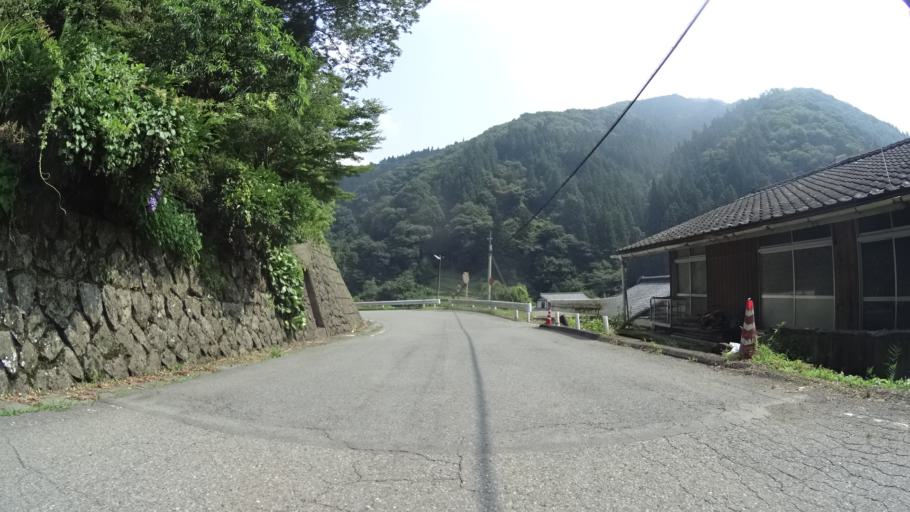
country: JP
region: Gunma
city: Tomioka
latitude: 36.0630
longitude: 138.8322
